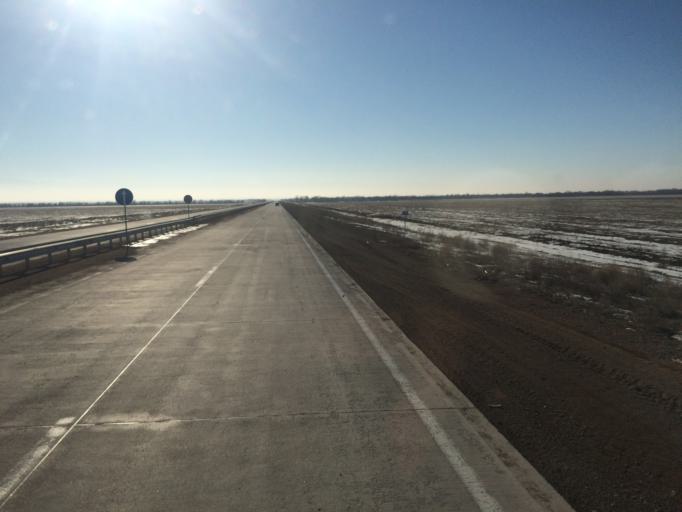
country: KG
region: Chuy
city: Sokuluk
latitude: 43.3383
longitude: 74.2837
